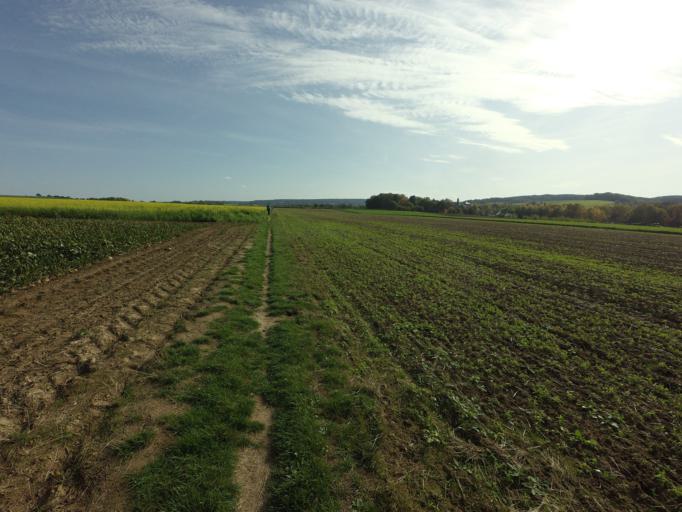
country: NL
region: Limburg
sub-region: Gemeente Voerendaal
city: Ubachsberg
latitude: 50.8185
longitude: 5.9123
